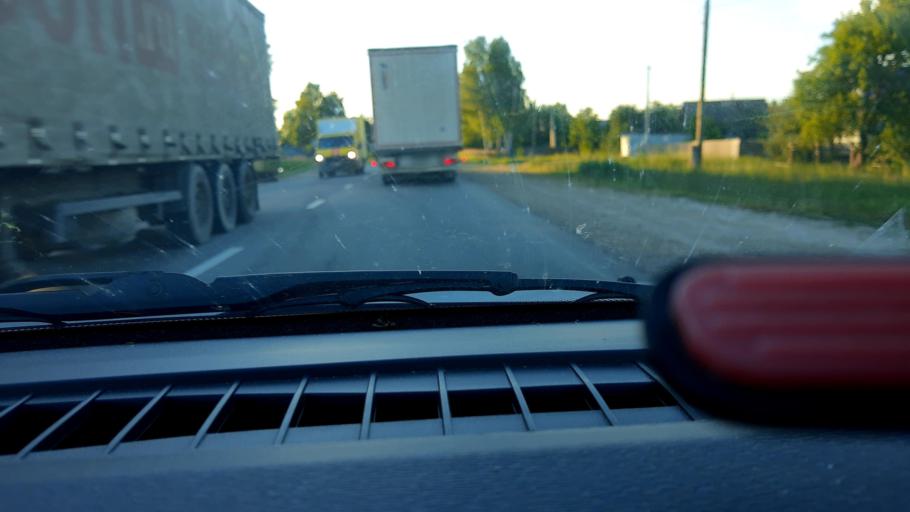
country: RU
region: Nizjnij Novgorod
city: Uren'
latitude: 57.3426
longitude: 45.7101
